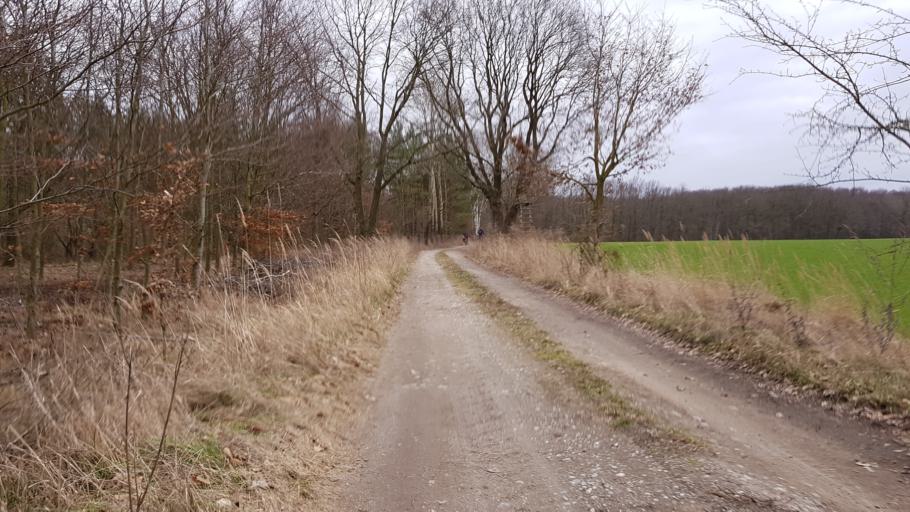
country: PL
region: West Pomeranian Voivodeship
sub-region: Powiat gryfinski
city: Banie
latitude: 53.0739
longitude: 14.7309
